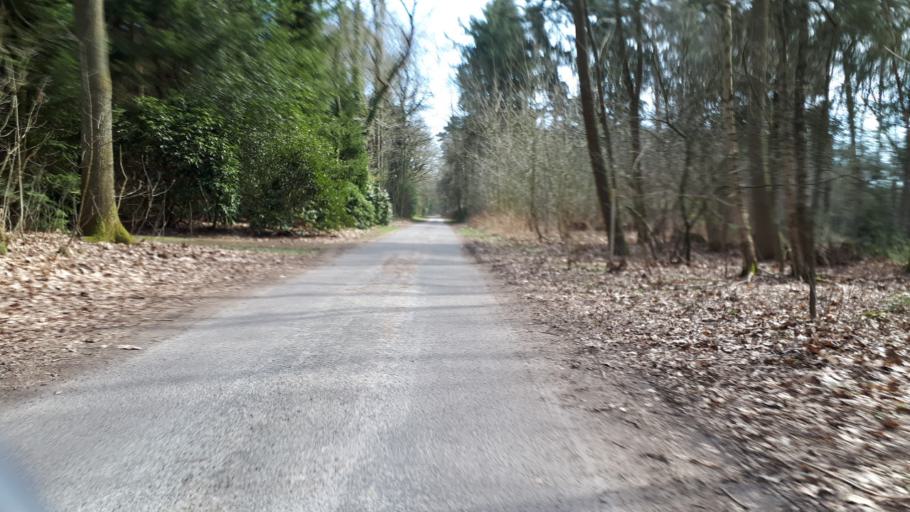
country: DE
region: Lower Saxony
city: Grossenkneten
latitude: 53.0098
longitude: 8.3027
